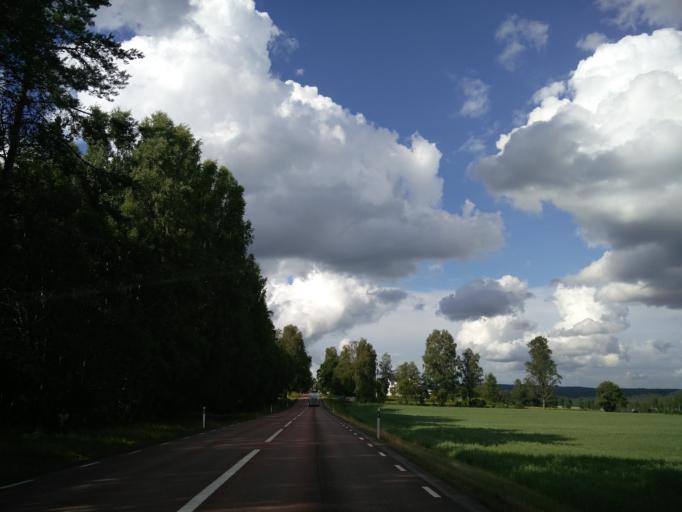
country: SE
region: Vaermland
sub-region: Torsby Kommun
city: Torsby
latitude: 60.2684
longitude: 13.0270
